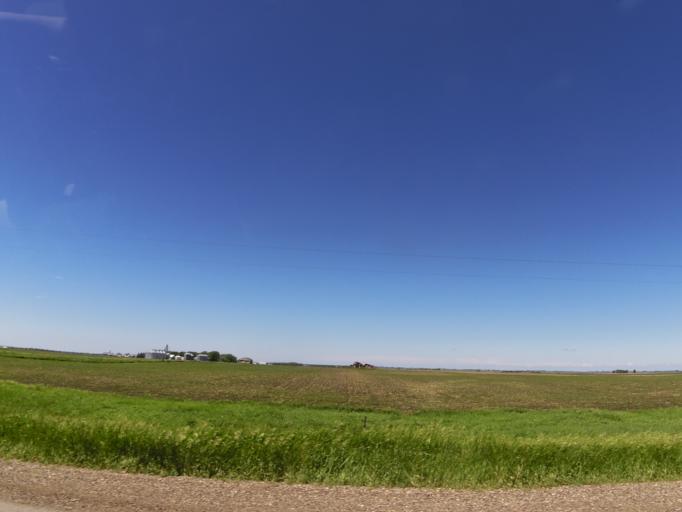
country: US
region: Minnesota
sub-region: Becker County
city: Detroit Lakes
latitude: 47.0103
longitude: -95.9124
